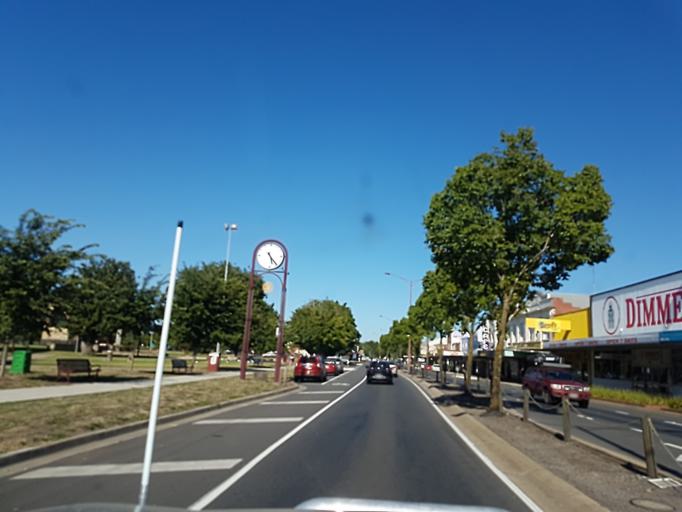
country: AU
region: Victoria
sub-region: Colac-Otway
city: Colac
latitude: -38.3396
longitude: 143.5872
